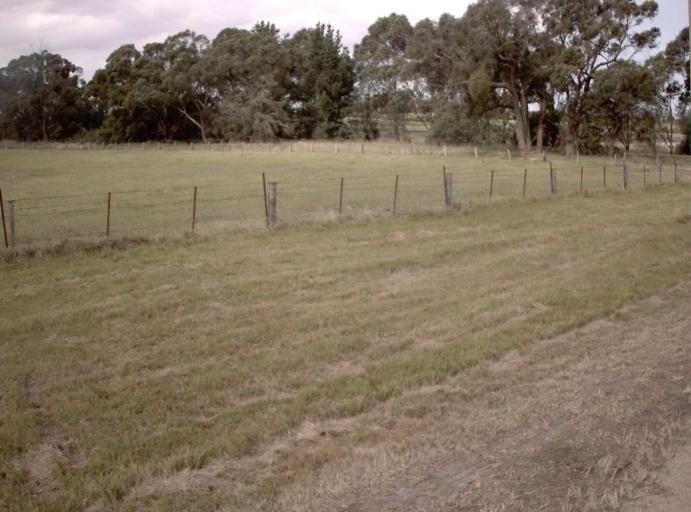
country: AU
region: Victoria
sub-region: Wellington
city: Sale
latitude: -38.2168
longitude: 147.1345
